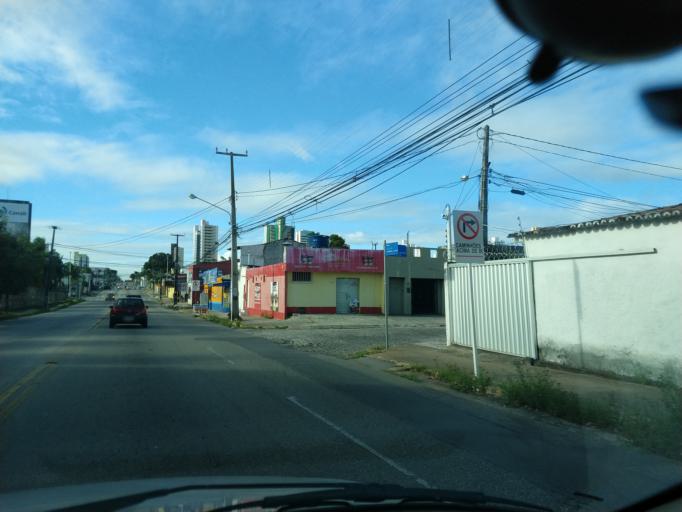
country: BR
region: Rio Grande do Norte
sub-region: Natal
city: Natal
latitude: -5.8248
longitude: -35.2205
